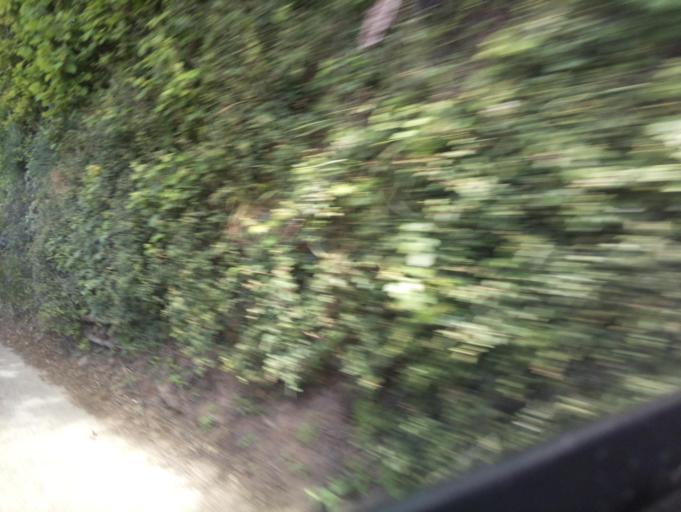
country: GB
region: England
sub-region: Devon
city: Uffculme
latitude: 50.8396
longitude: -3.3046
